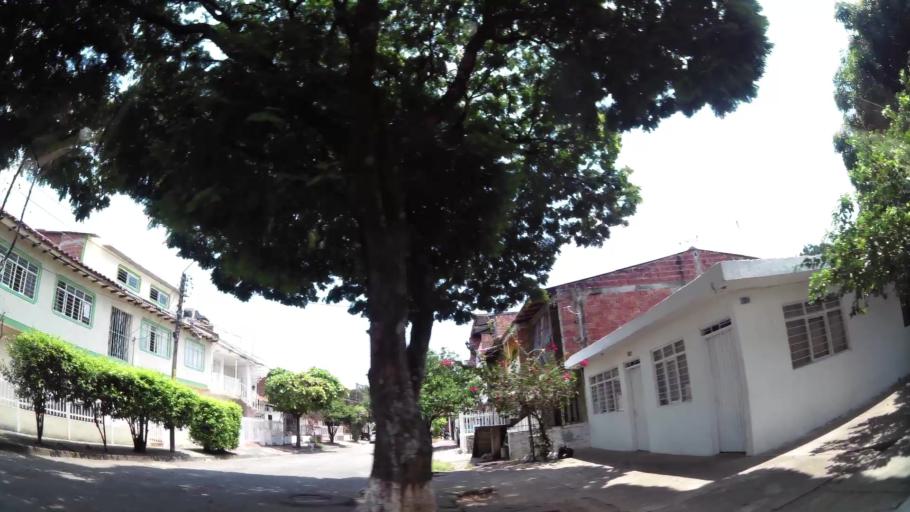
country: CO
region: Valle del Cauca
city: Cali
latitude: 3.4094
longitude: -76.5322
